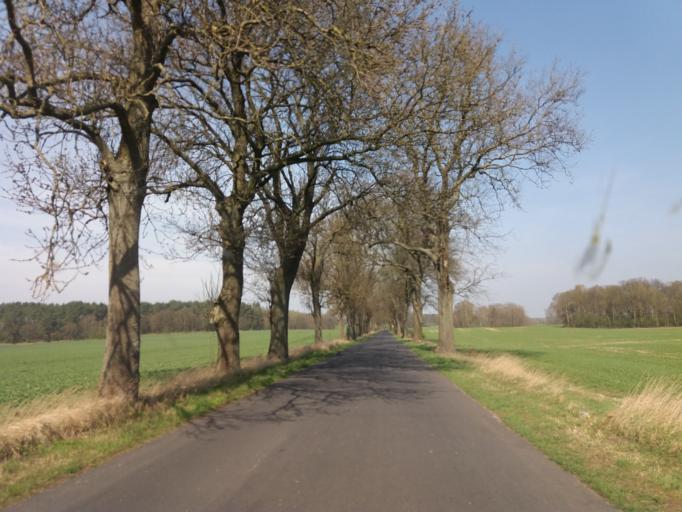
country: PL
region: West Pomeranian Voivodeship
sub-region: Powiat choszczenski
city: Recz
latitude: 53.2338
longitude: 15.6045
